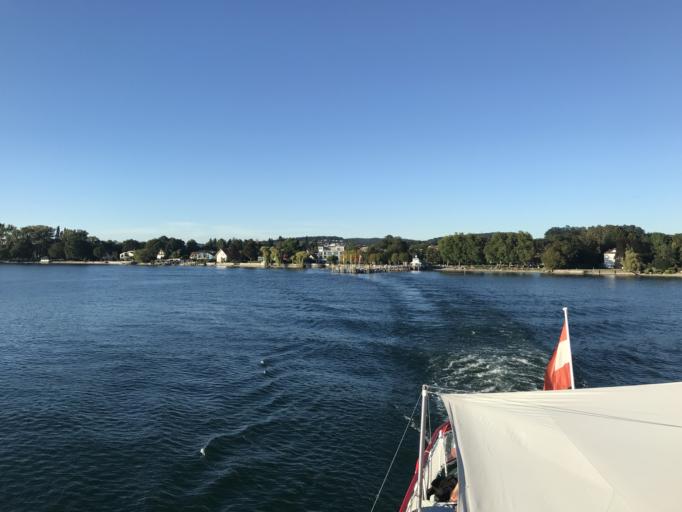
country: DE
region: Baden-Wuerttemberg
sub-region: Tuebingen Region
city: Kressbronn am Bodensee
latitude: 47.5834
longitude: 9.5981
